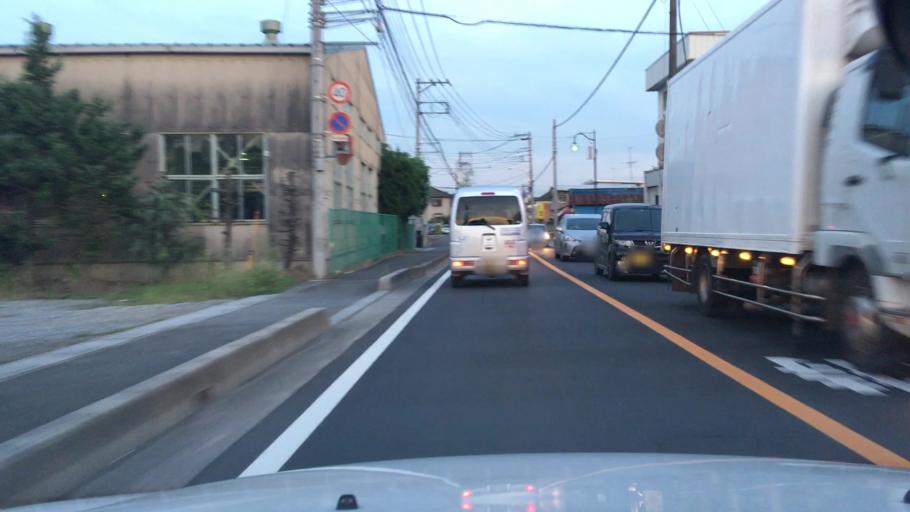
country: JP
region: Saitama
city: Kasukabe
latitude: 35.9340
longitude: 139.7355
